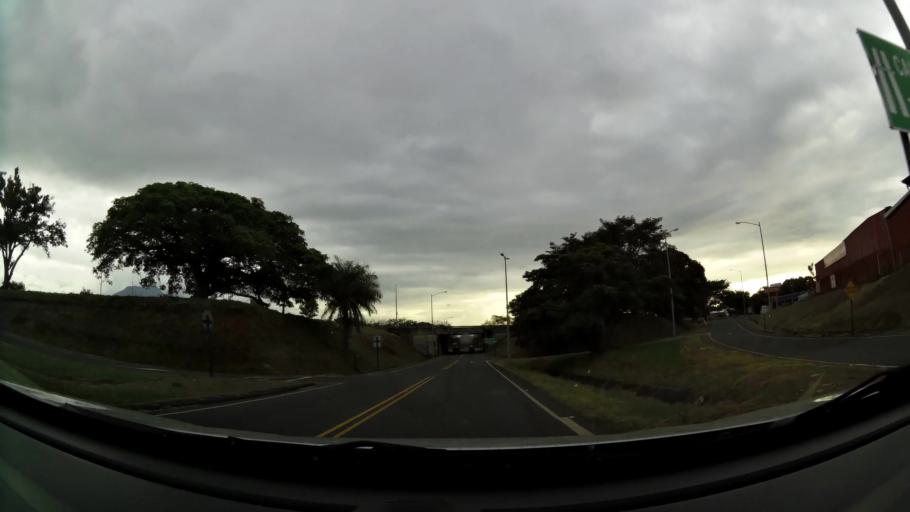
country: CR
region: Alajuela
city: Orotina
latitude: 9.9077
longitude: -84.5202
